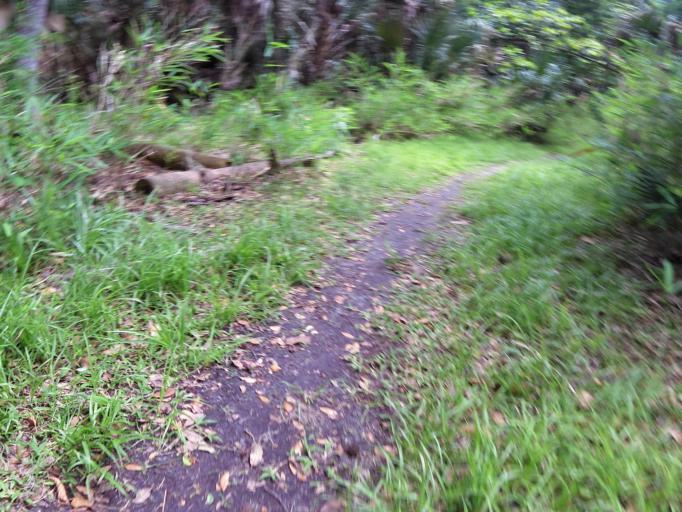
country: US
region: Florida
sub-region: Flagler County
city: Flagler Beach
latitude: 29.4210
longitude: -81.1399
